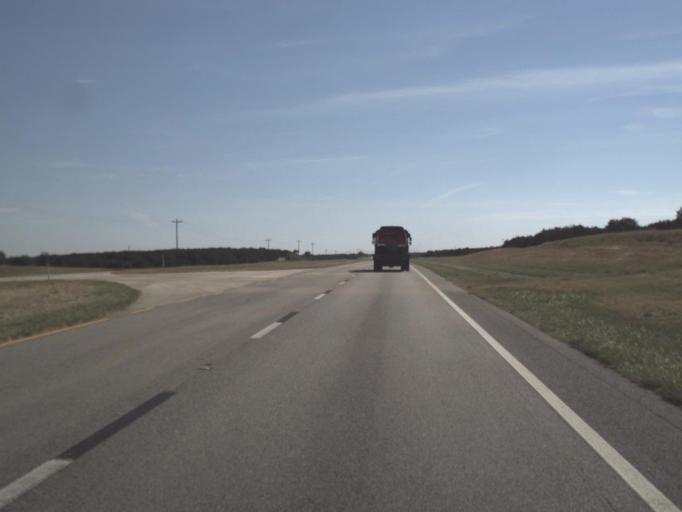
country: US
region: Florida
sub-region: Highlands County
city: Placid Lakes
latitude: 27.1843
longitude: -81.3288
